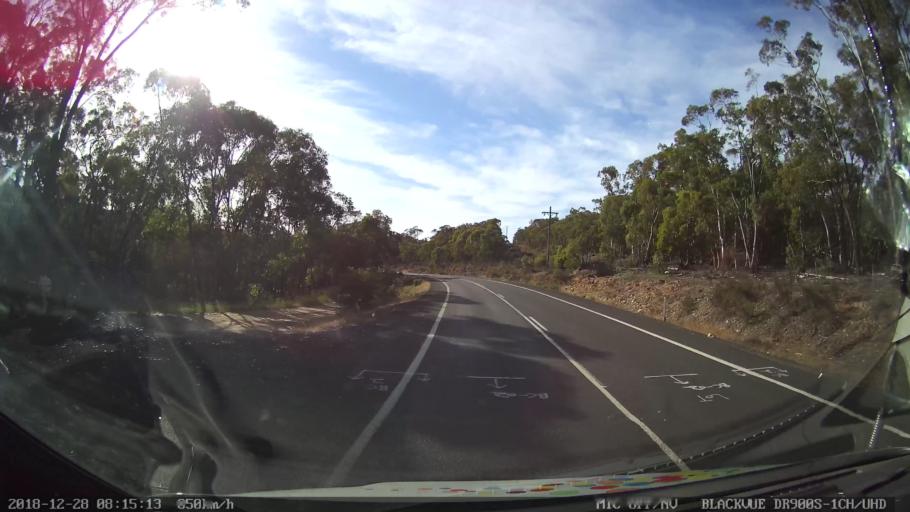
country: AU
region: New South Wales
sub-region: Blayney
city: Blayney
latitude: -33.8222
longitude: 149.3268
